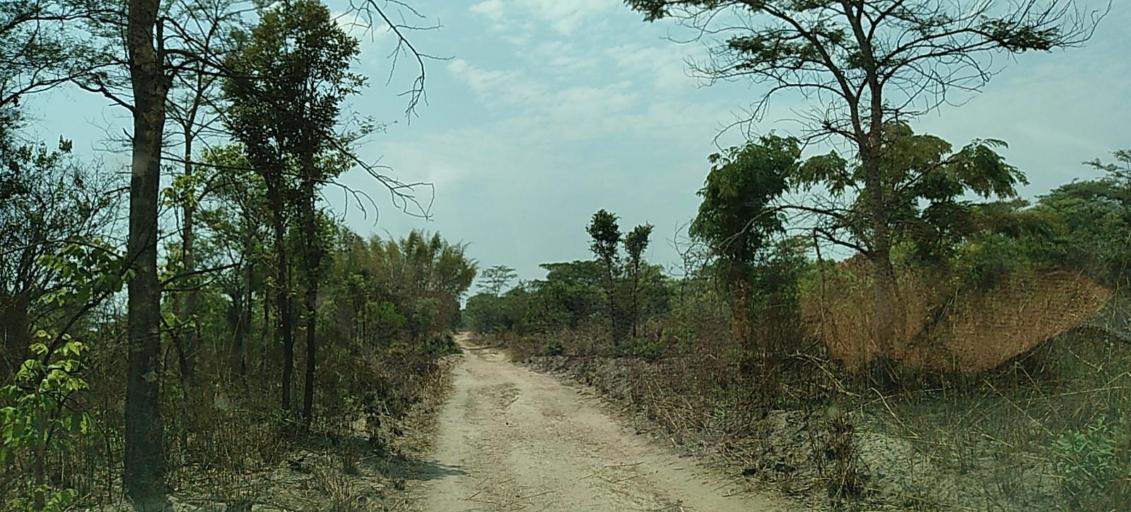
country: ZM
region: Copperbelt
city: Kalulushi
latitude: -12.9476
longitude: 28.1303
